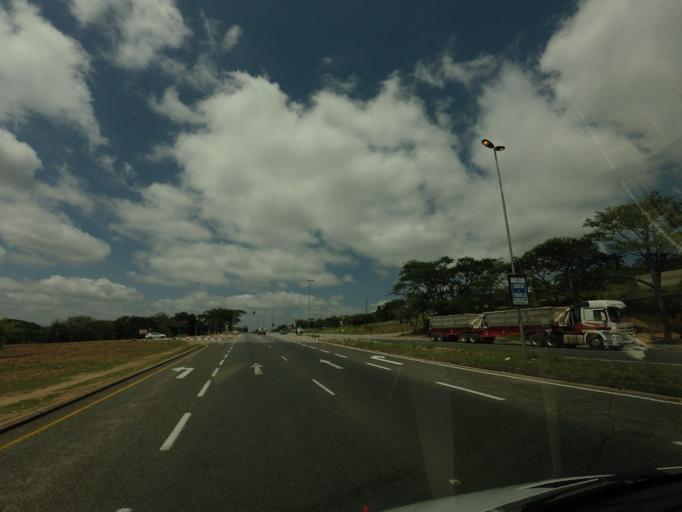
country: ZA
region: Mpumalanga
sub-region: Ehlanzeni District
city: Nelspruit
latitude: -25.4048
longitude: 30.9821
